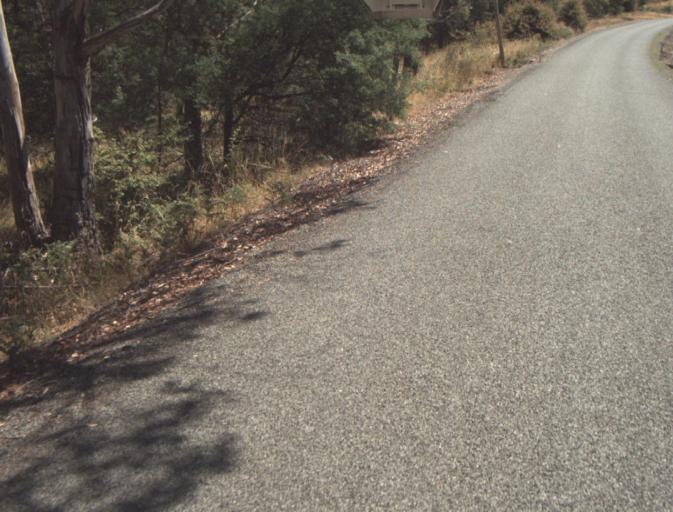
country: AU
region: Tasmania
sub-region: Launceston
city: Newstead
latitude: -41.3597
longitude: 147.3021
